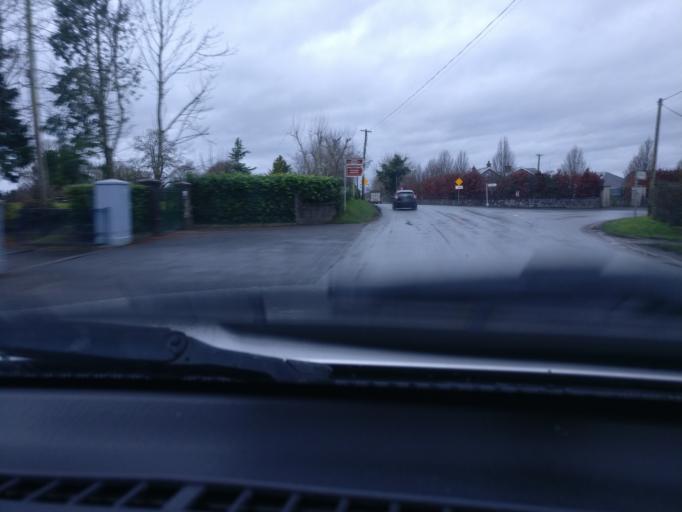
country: IE
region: Leinster
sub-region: An Mhi
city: Longwood
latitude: 53.4546
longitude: -6.9384
